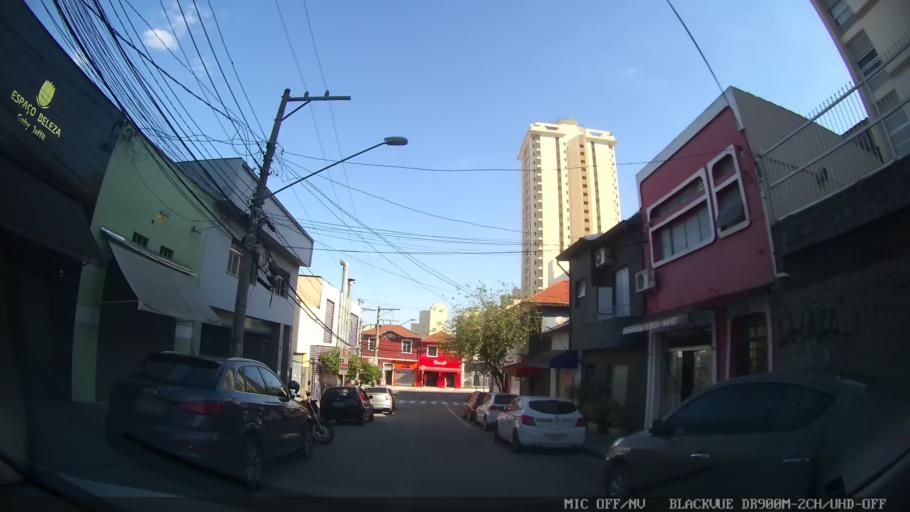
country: BR
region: Sao Paulo
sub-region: Sao Paulo
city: Sao Paulo
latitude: -23.4999
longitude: -46.6264
